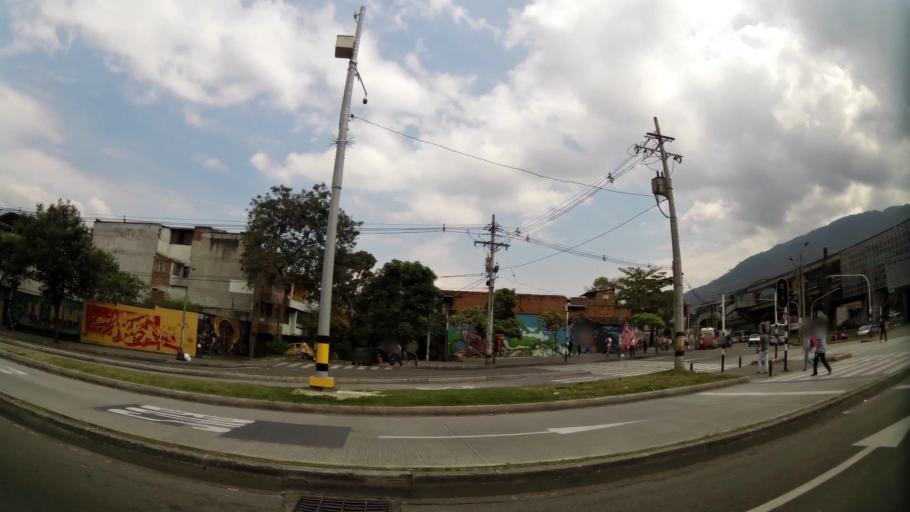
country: CO
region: Antioquia
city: Medellin
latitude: 6.2639
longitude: -75.5640
